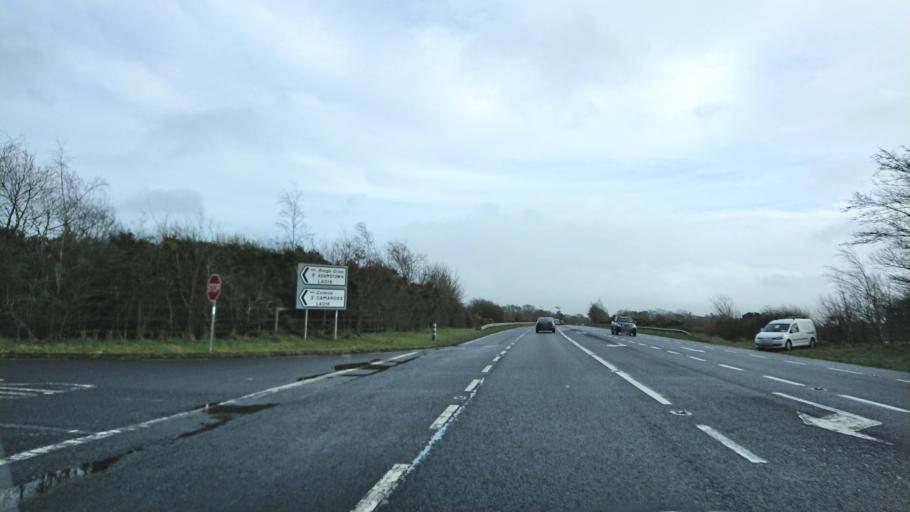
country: IE
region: Leinster
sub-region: Loch Garman
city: Enniscorthy
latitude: 52.3612
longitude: -6.7152
